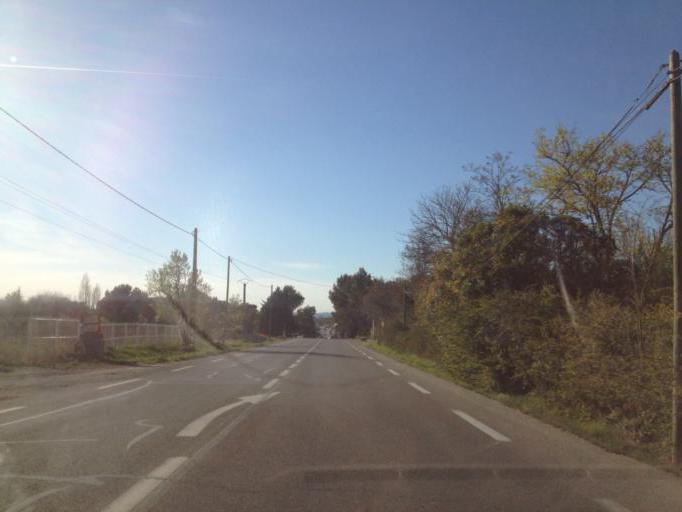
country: FR
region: Provence-Alpes-Cote d'Azur
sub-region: Departement des Bouches-du-Rhone
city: Saint-Cannat
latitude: 43.6090
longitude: 5.3305
